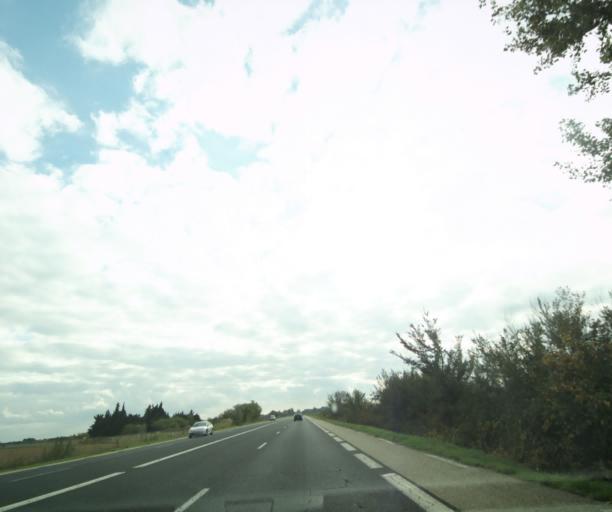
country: FR
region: Languedoc-Roussillon
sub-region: Departement de l'Herault
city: Marsillargues
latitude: 43.6554
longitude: 4.2023
